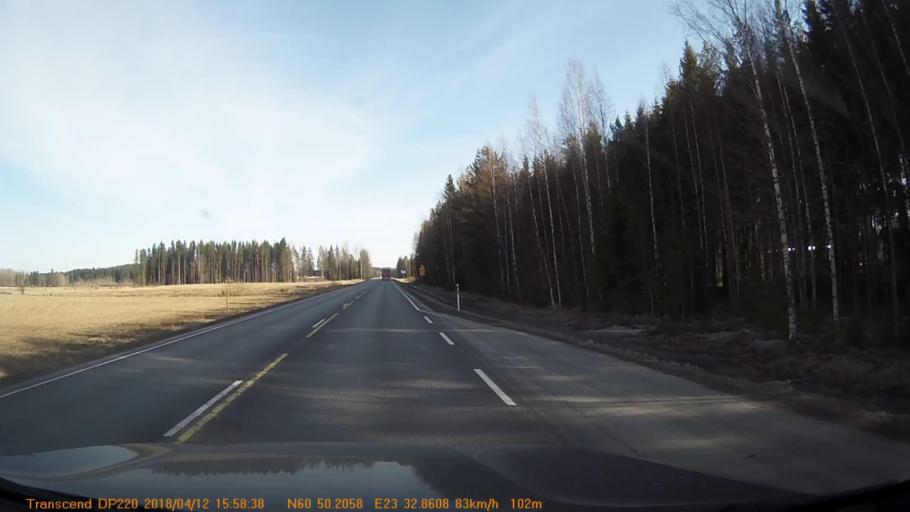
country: FI
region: Haeme
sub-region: Forssa
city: Forssa
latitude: 60.8362
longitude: 23.5489
